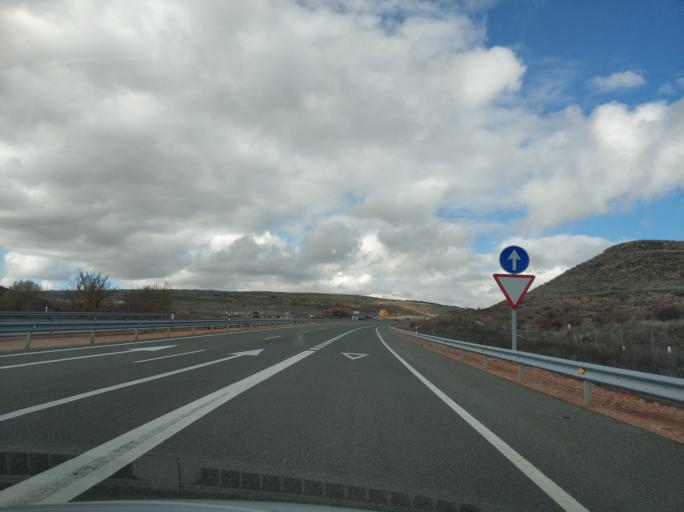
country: ES
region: Castille and Leon
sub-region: Provincia de Soria
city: Medinaceli
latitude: 41.1765
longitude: -2.4241
